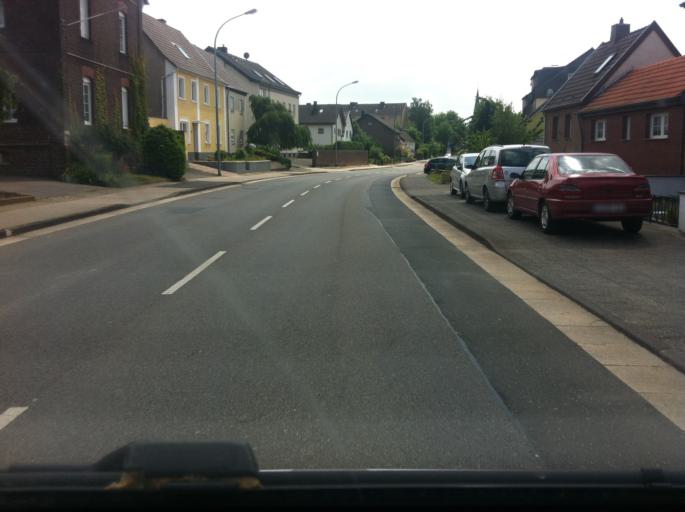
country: DE
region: North Rhine-Westphalia
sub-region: Regierungsbezirk Koln
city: Weilerswist
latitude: 50.7441
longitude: 6.8370
